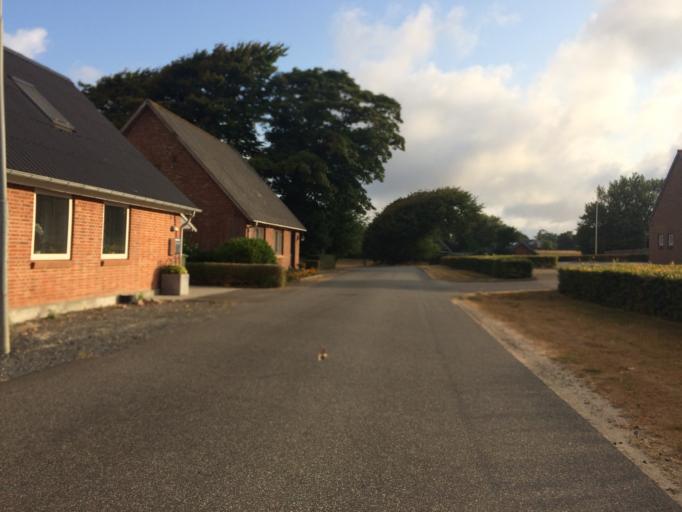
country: DK
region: Central Jutland
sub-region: Holstebro Kommune
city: Vinderup
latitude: 56.5963
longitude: 8.7312
